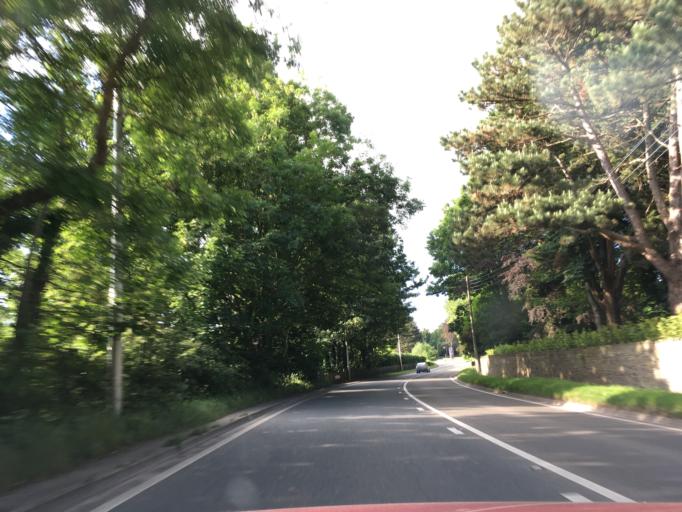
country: GB
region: England
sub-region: North Somerset
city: Winscombe
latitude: 51.3043
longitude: -2.8277
